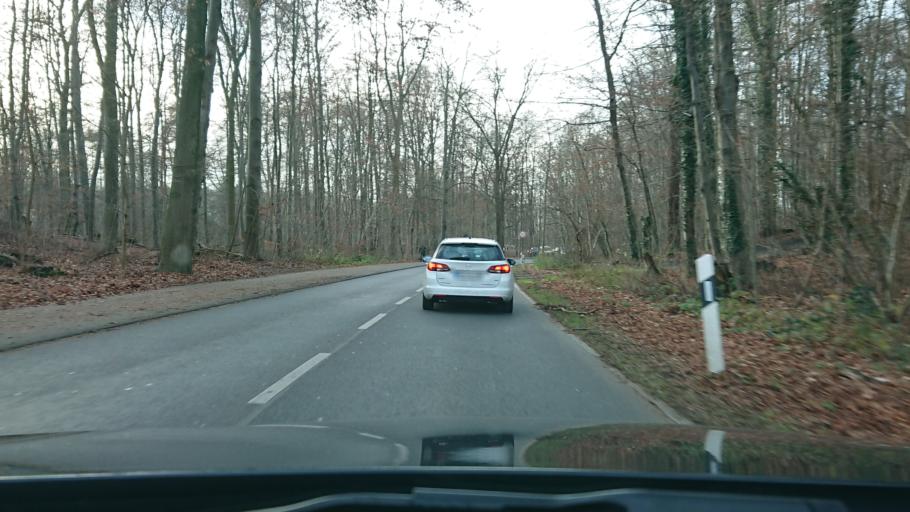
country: DE
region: North Rhine-Westphalia
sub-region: Regierungsbezirk Koln
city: Hurth
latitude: 50.9107
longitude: 6.8889
